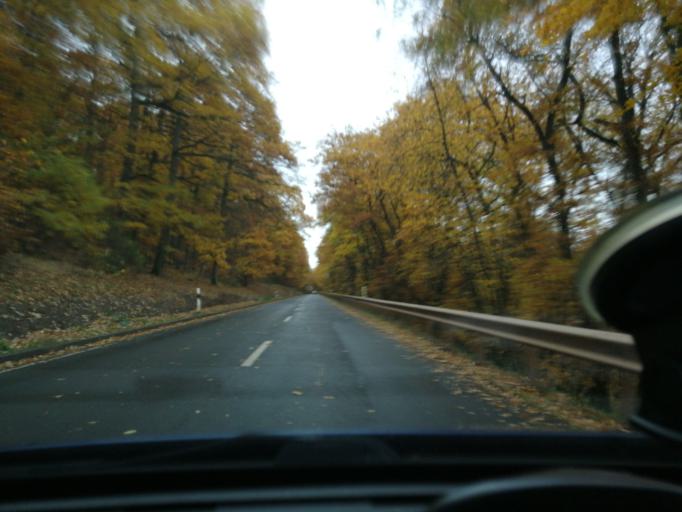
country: DE
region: Rheinland-Pfalz
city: Klausen
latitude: 49.8921
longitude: 6.8911
